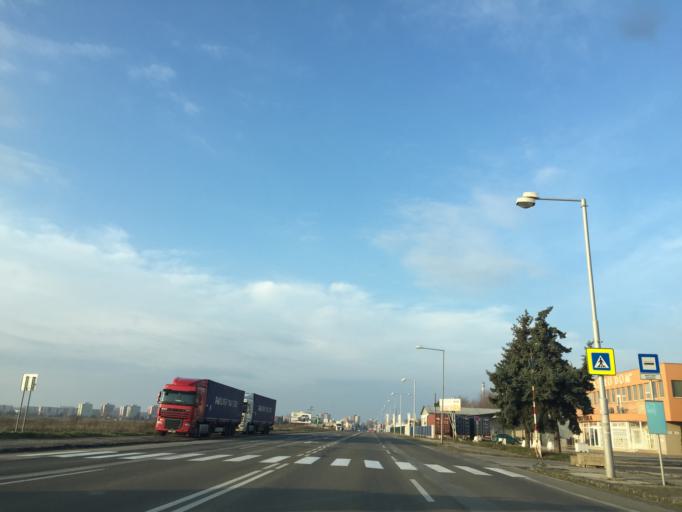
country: SK
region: Nitriansky
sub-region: Okres Nove Zamky
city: Nove Zamky
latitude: 47.9700
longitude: 18.1830
